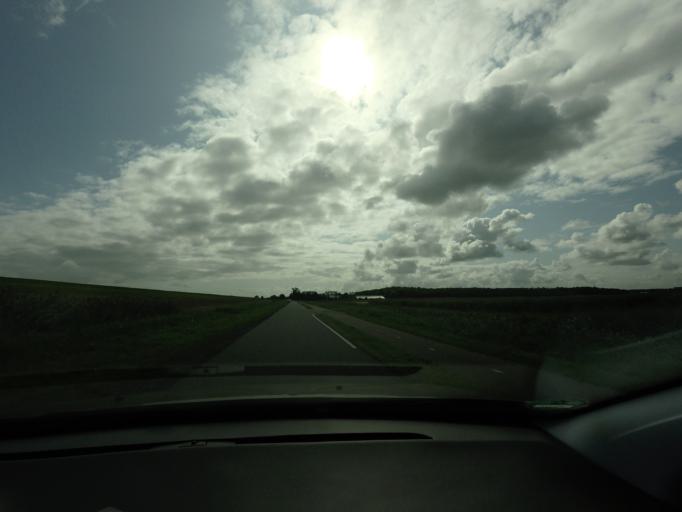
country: NL
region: North Holland
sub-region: Gemeente Hollands Kroon
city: Den Oever
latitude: 52.9015
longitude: 5.0661
